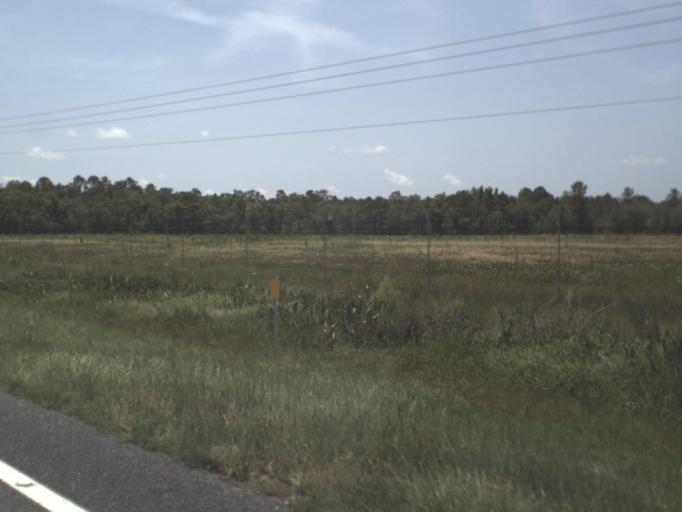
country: US
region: Florida
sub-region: Taylor County
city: Steinhatchee
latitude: 29.8242
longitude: -83.3557
